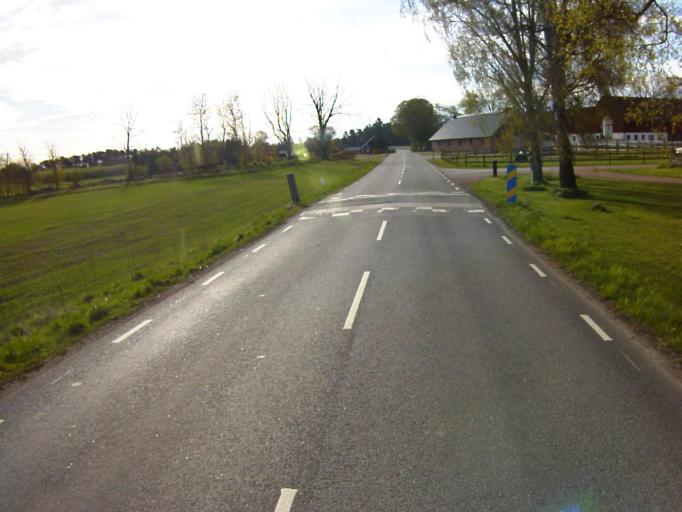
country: SE
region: Skane
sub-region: Kristianstads Kommun
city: Norra Asum
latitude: 55.9926
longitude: 14.1298
